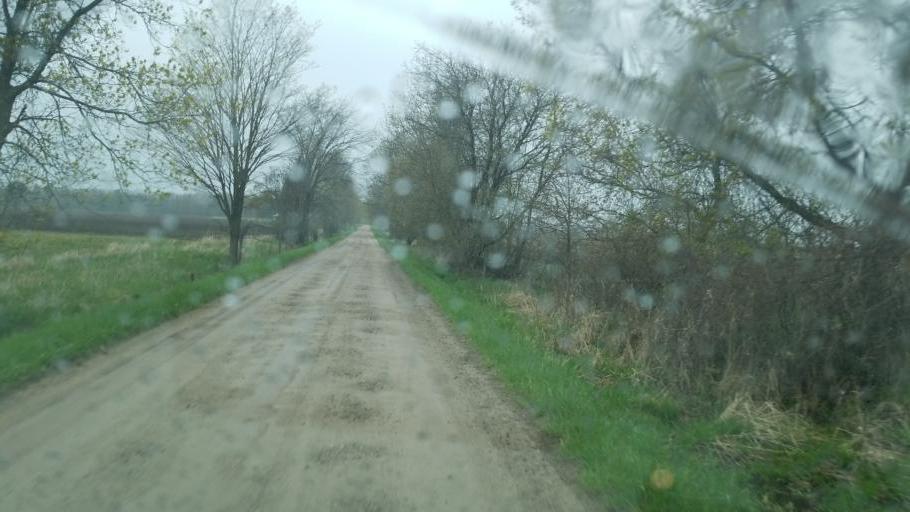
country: US
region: Michigan
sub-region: Mecosta County
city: Canadian Lakes
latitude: 43.5110
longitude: -85.3051
